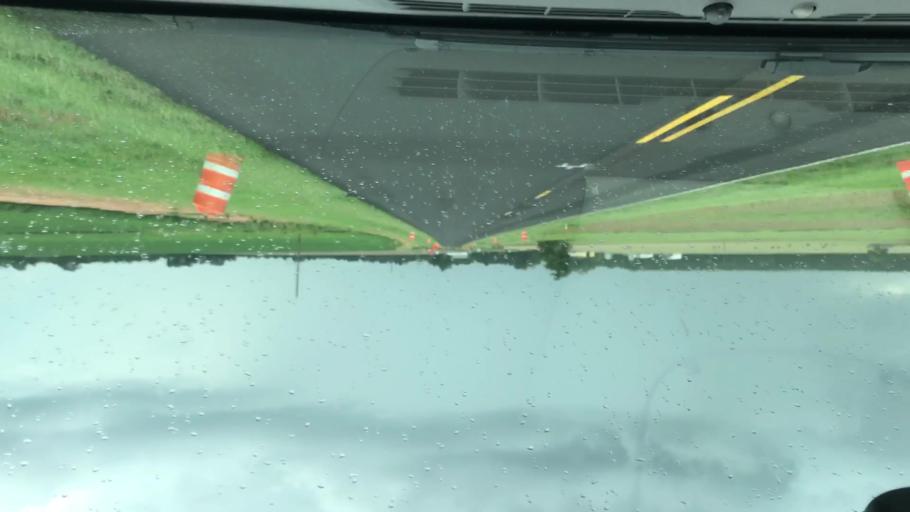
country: US
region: Georgia
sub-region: Clay County
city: Fort Gaines
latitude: 31.4970
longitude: -85.0187
